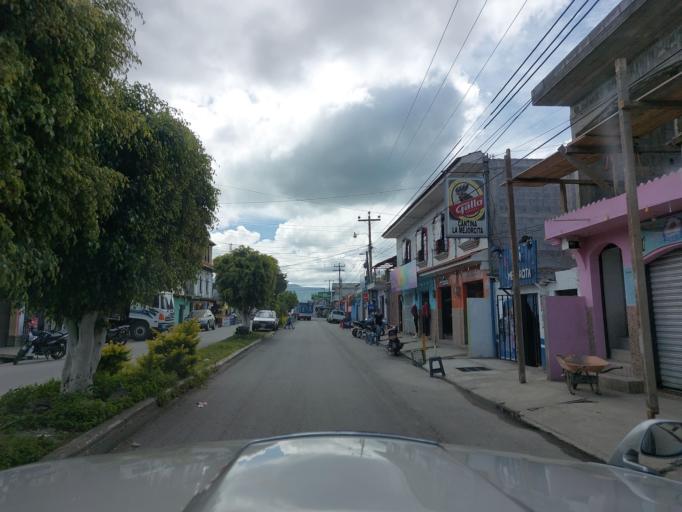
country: GT
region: Chimaltenango
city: Parramos
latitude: 14.6090
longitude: -90.8039
